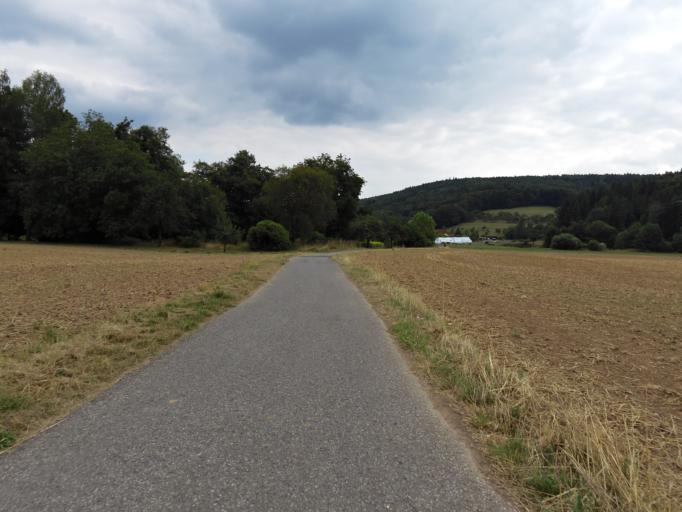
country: DE
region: Bavaria
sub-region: Regierungsbezirk Unterfranken
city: Momlingen
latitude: 49.8455
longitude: 9.0890
